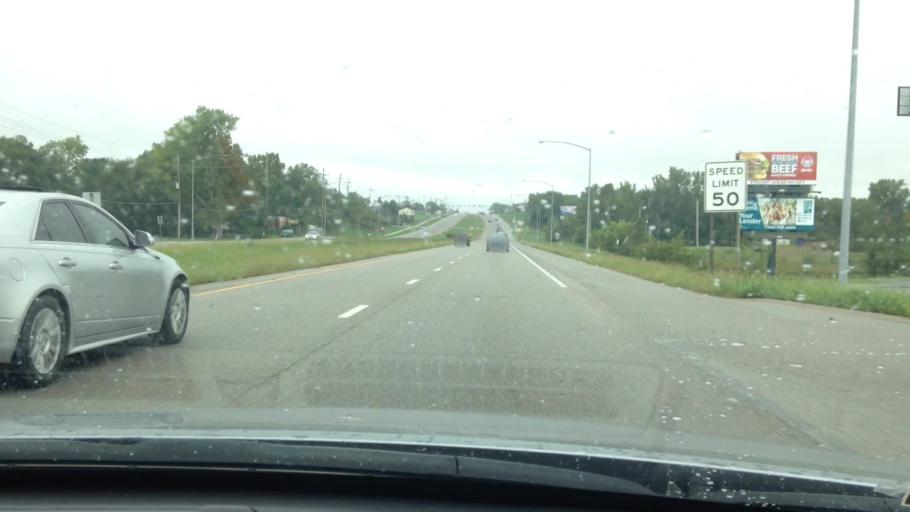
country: US
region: Kansas
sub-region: Leavenworth County
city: Lansing
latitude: 39.2312
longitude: -94.8997
